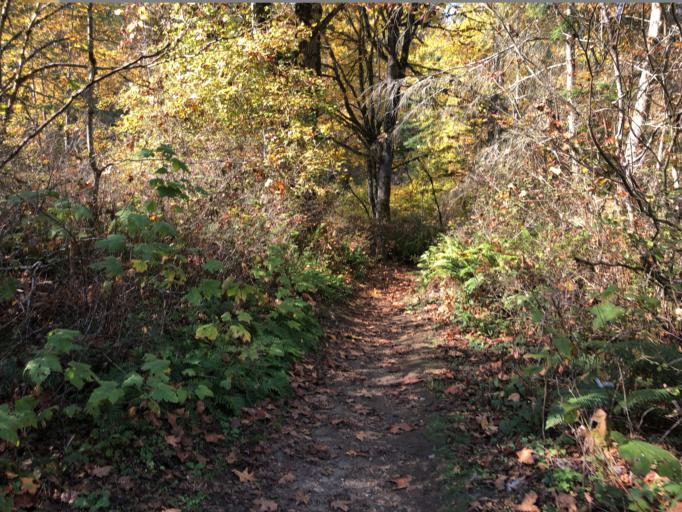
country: US
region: Washington
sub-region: King County
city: Ravensdale
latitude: 47.3218
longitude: -121.9082
